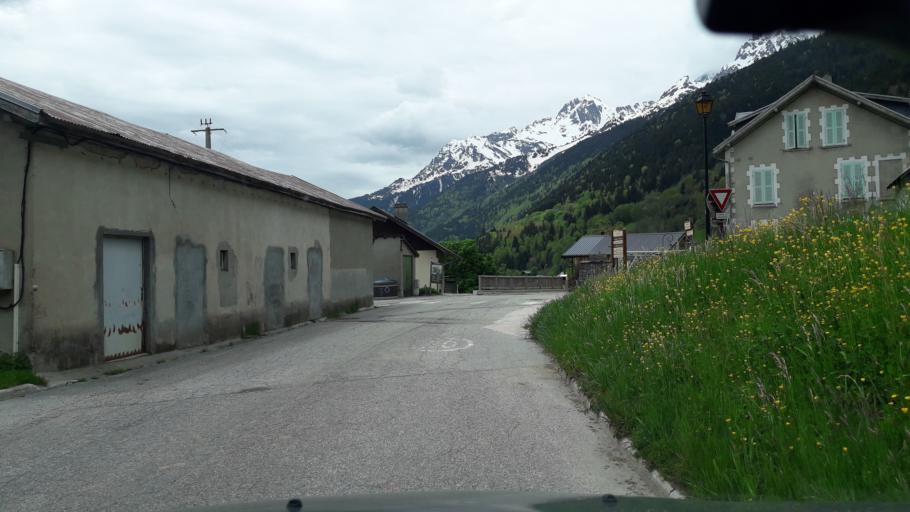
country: FR
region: Rhone-Alpes
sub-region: Departement de l'Isere
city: Theys
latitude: 45.2054
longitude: 6.0435
